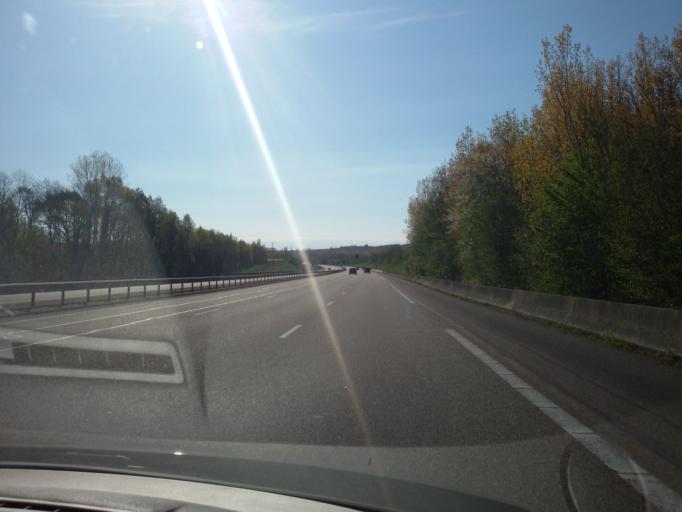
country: FR
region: Bourgogne
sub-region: Departement de l'Yonne
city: Fleury-la-Vallee
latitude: 47.8855
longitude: 3.4239
